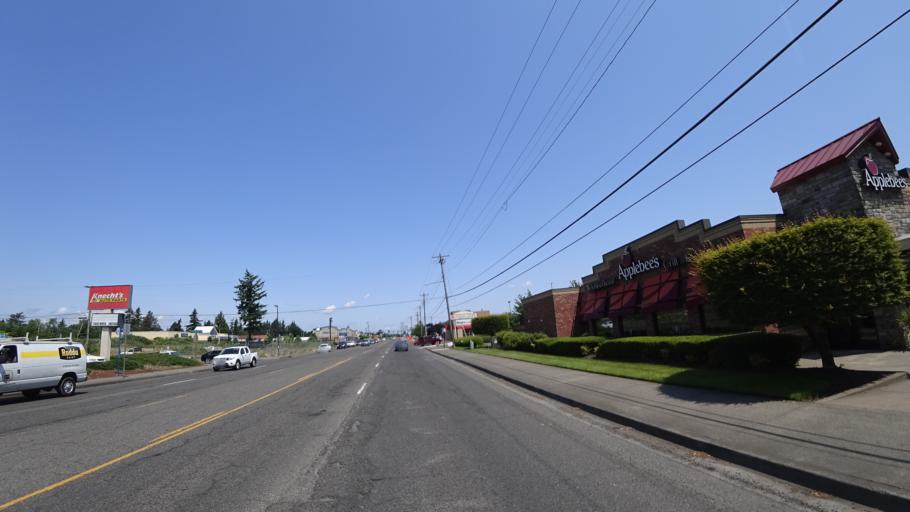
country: US
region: Oregon
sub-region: Multnomah County
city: Lents
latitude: 45.4490
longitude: -122.5789
